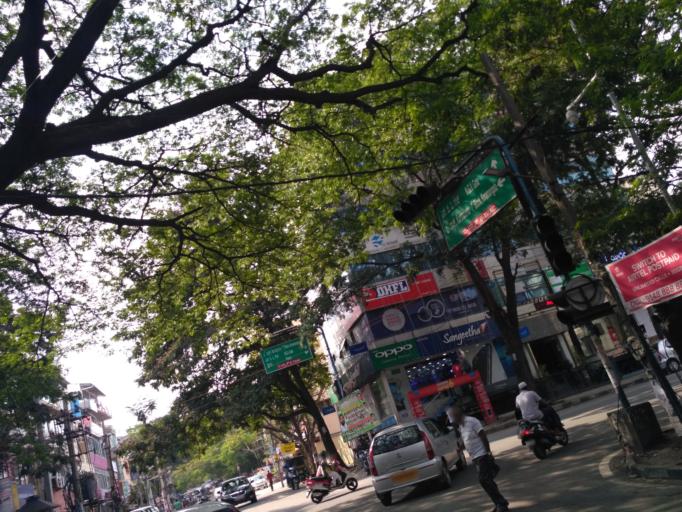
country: IN
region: Karnataka
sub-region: Bangalore Urban
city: Bangalore
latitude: 12.9357
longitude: 77.6154
